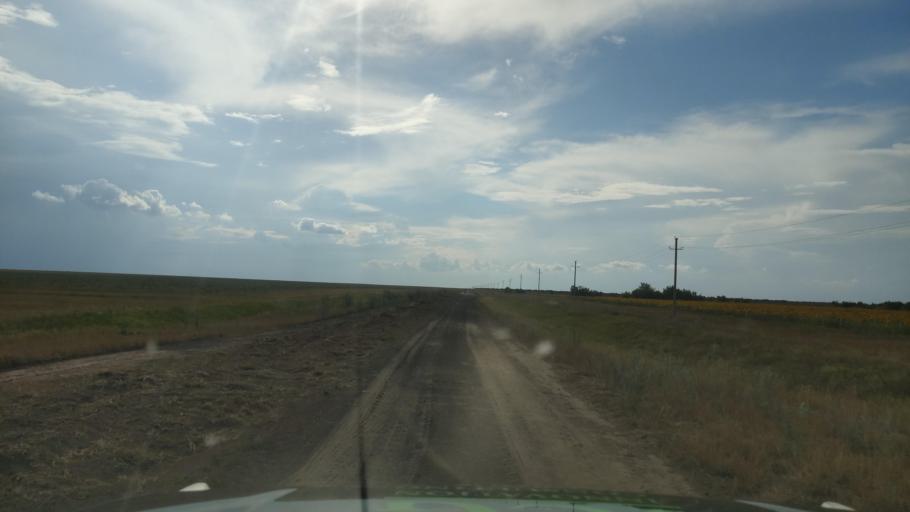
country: KZ
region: Pavlodar
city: Pavlodar
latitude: 52.5122
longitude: 77.5453
